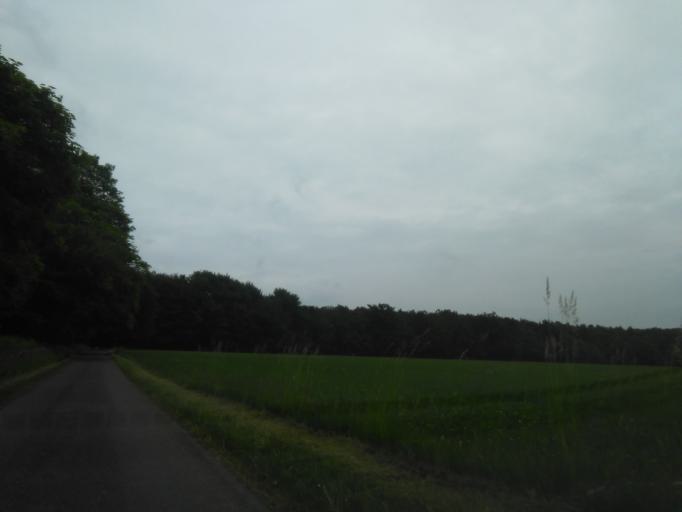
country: DK
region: Capital Region
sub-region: Bornholm Kommune
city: Akirkeby
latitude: 55.1159
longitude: 14.9275
